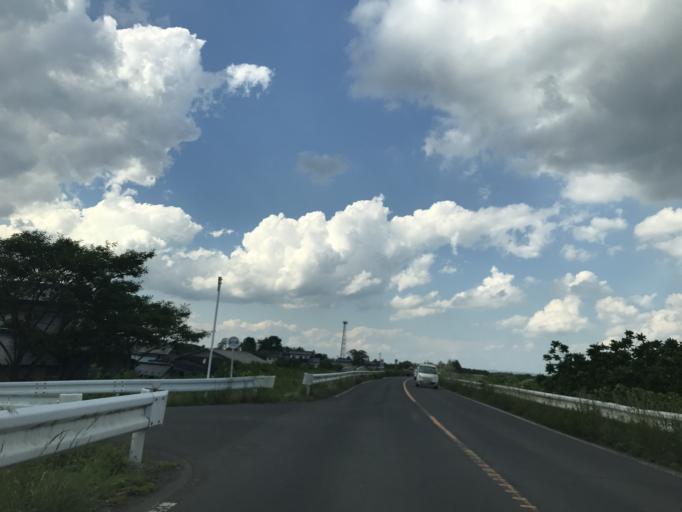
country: JP
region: Miyagi
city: Wakuya
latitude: 38.6363
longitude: 141.2044
